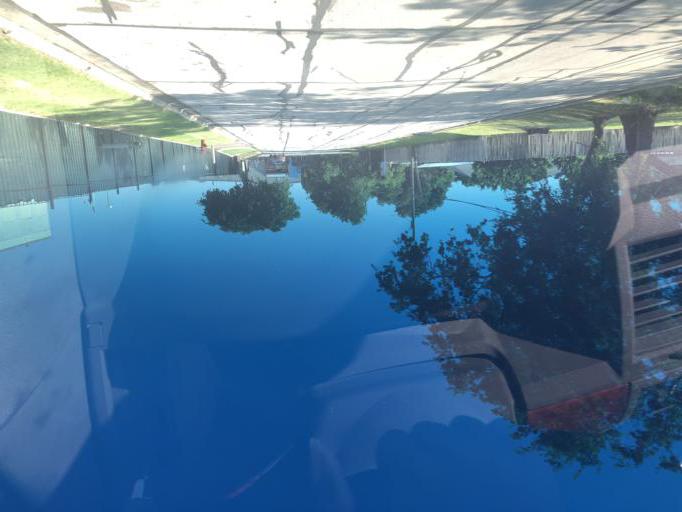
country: US
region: Texas
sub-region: Dallas County
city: Grand Prairie
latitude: 32.7304
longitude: -97.0402
